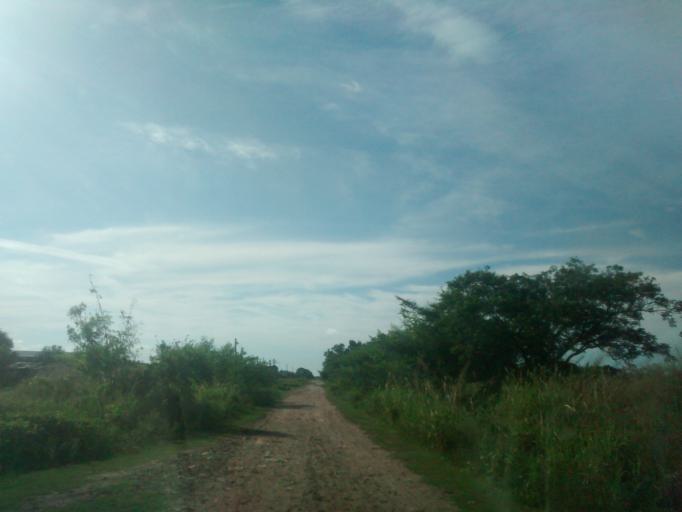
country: AR
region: Chaco
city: Puerto Tirol
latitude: -27.3783
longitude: -59.0966
